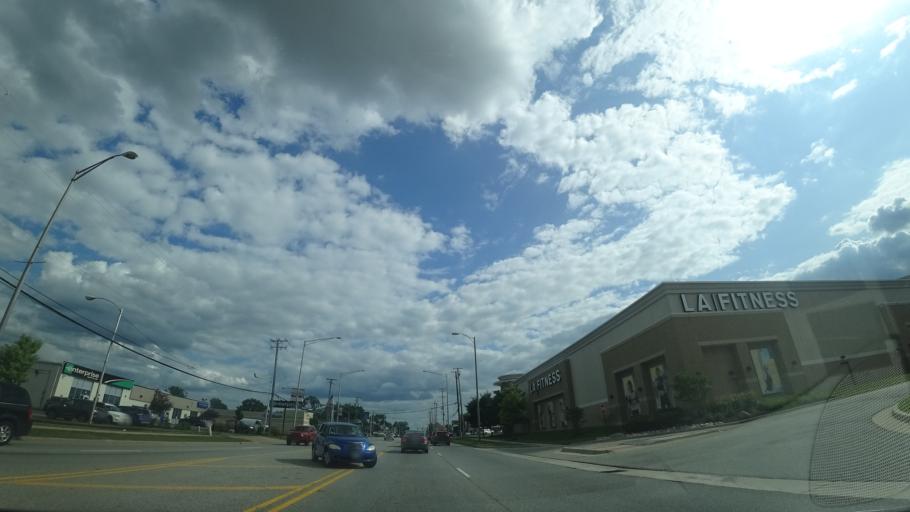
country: US
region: Illinois
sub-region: Cook County
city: Alsip
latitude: 41.6737
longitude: -87.7391
